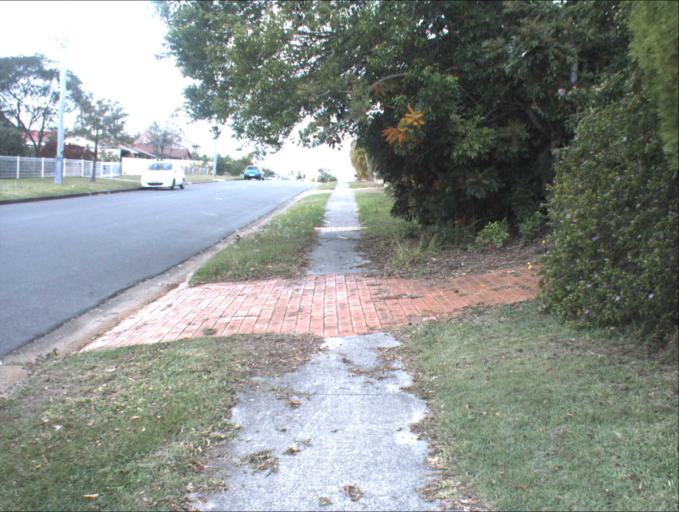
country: AU
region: Queensland
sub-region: Brisbane
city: Sunnybank Hills
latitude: -27.6662
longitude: 153.0381
